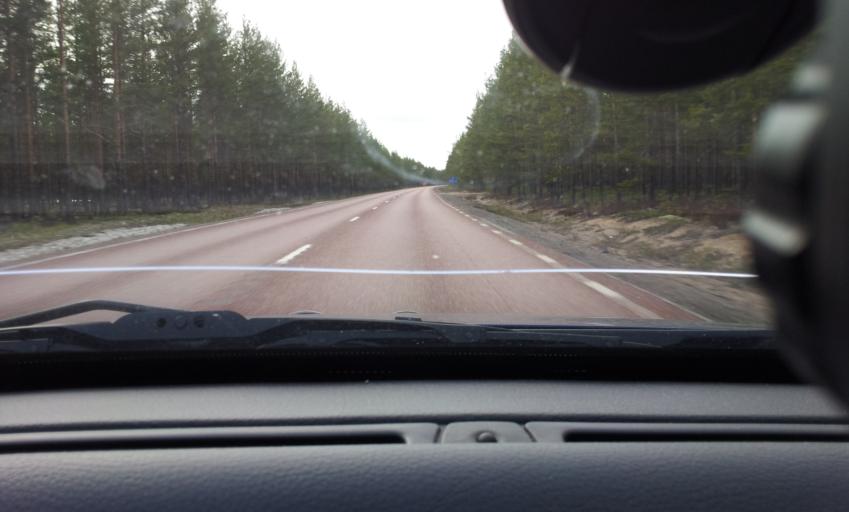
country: SE
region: Gaevleborg
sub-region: Ljusdals Kommun
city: Farila
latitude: 61.8901
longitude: 15.6686
